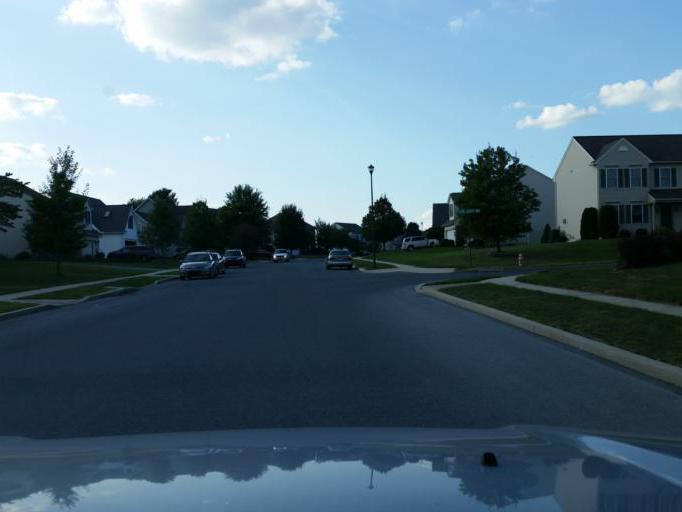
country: US
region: Pennsylvania
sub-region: Lebanon County
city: Campbelltown
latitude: 40.2814
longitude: -76.5862
